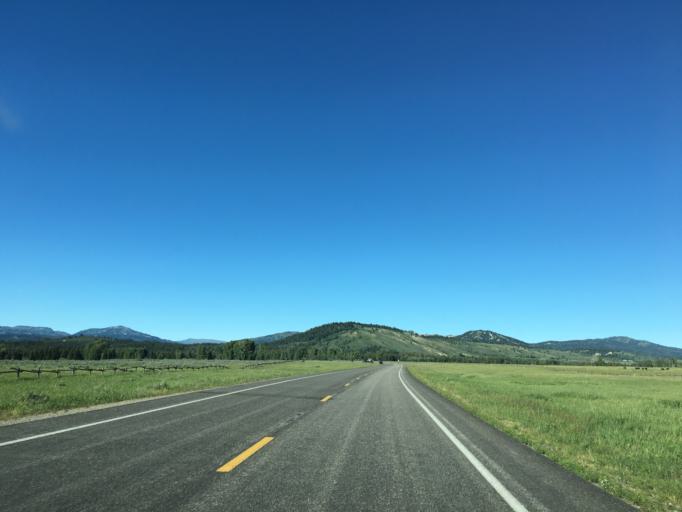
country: US
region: Wyoming
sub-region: Teton County
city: Jackson
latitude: 43.8229
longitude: -110.5202
